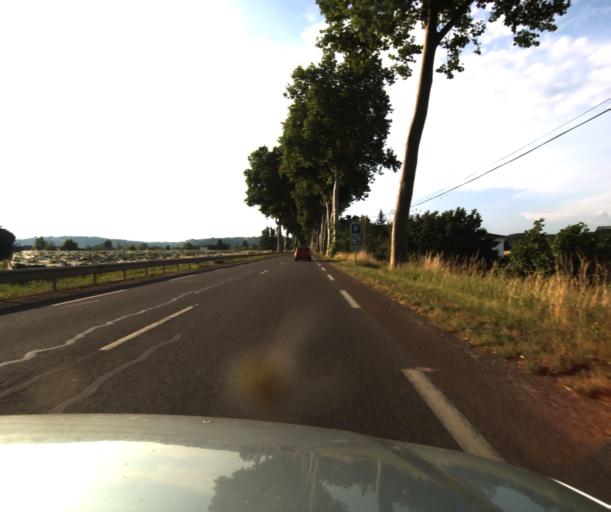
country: FR
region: Midi-Pyrenees
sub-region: Departement du Tarn-et-Garonne
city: Moissac
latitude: 44.0848
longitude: 1.0897
